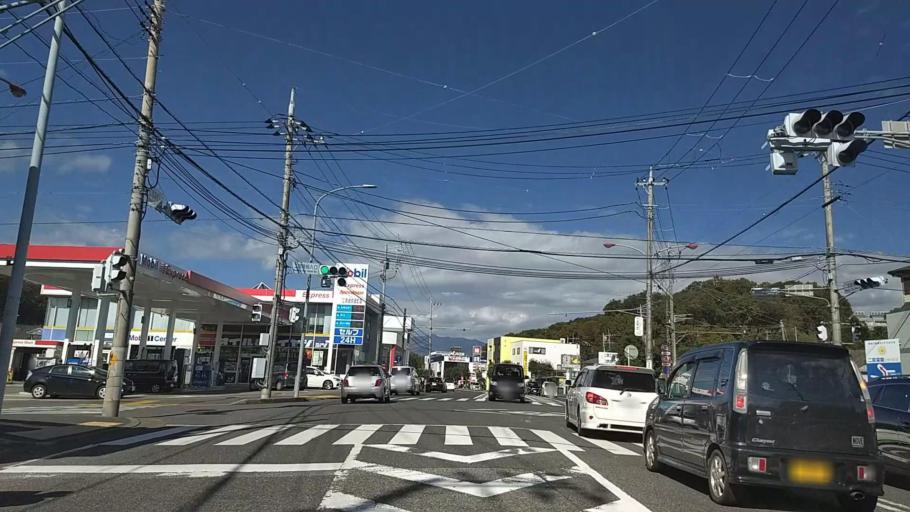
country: JP
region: Kanagawa
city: Ninomiya
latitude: 35.3130
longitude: 139.2445
